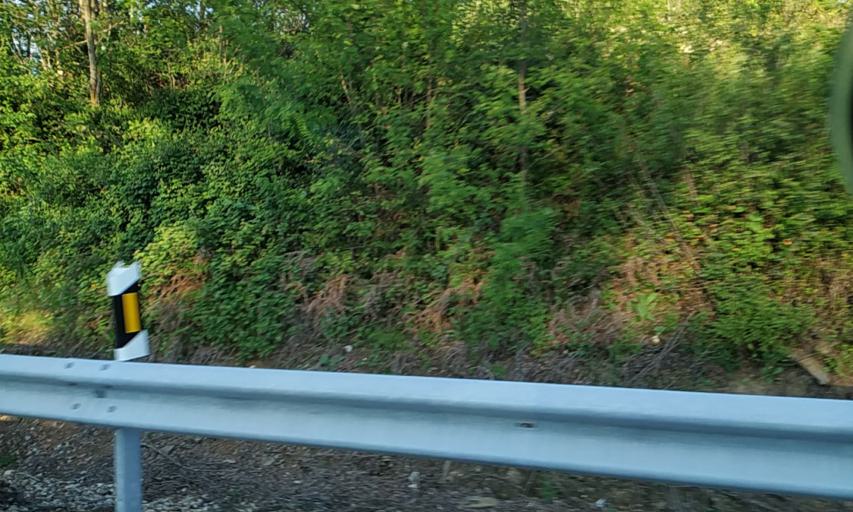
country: PT
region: Portalegre
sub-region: Portalegre
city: Sao Juliao
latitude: 39.3473
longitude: -7.2755
